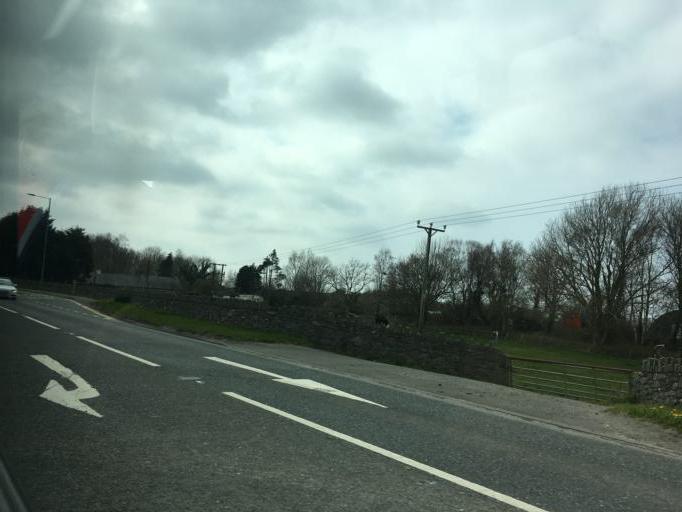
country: GB
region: Wales
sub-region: Gwynedd
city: Caernarfon
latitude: 53.1656
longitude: -4.2424
